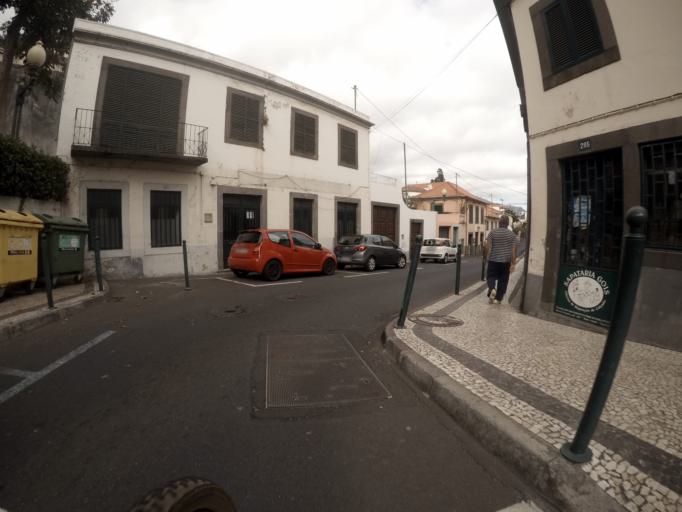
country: PT
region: Madeira
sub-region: Funchal
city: Funchal
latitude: 32.6493
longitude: -16.9179
